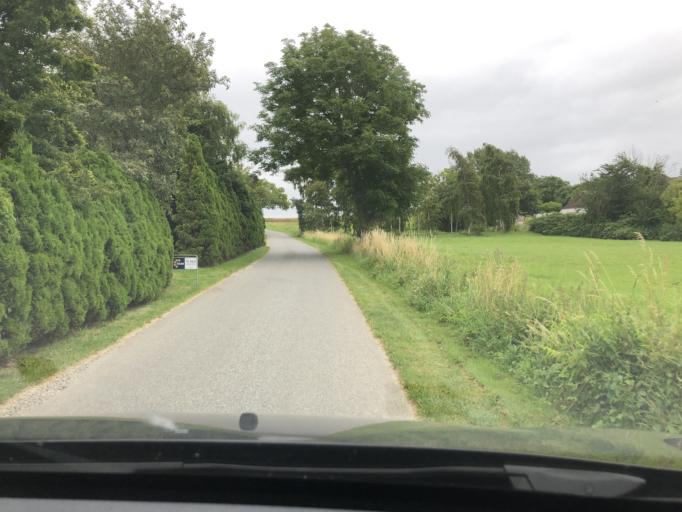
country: DK
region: South Denmark
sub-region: AEro Kommune
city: AEroskobing
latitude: 54.8342
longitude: 10.4240
